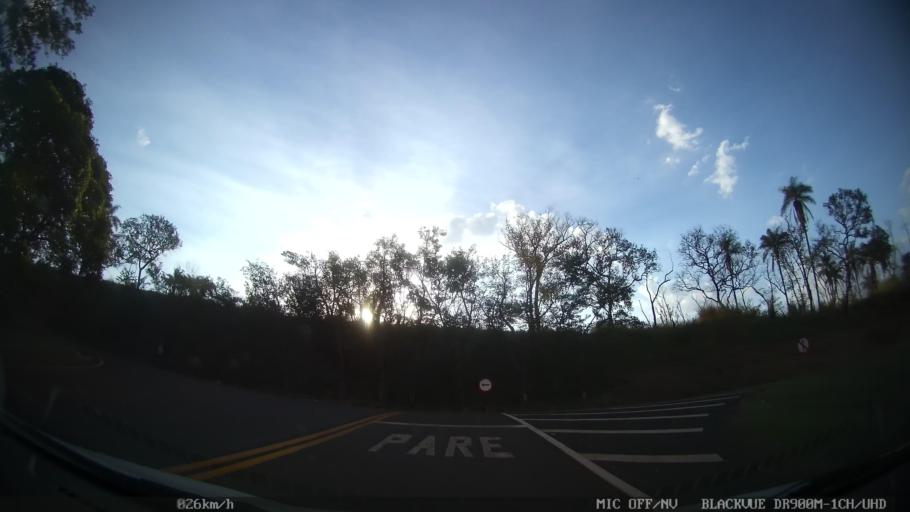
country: BR
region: Sao Paulo
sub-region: Jardinopolis
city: Jardinopolis
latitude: -21.1021
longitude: -47.7661
